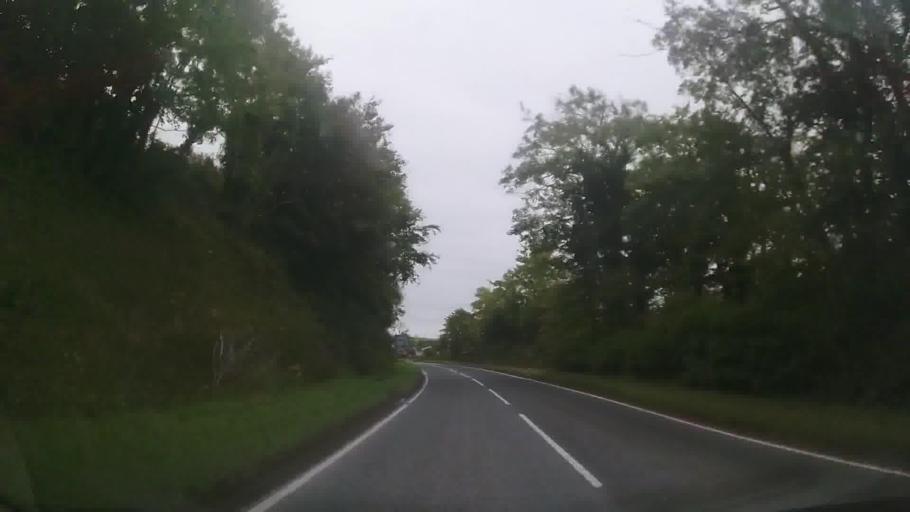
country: GB
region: Wales
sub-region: Carmarthenshire
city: Saint Clears
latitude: 51.7593
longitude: -4.4834
